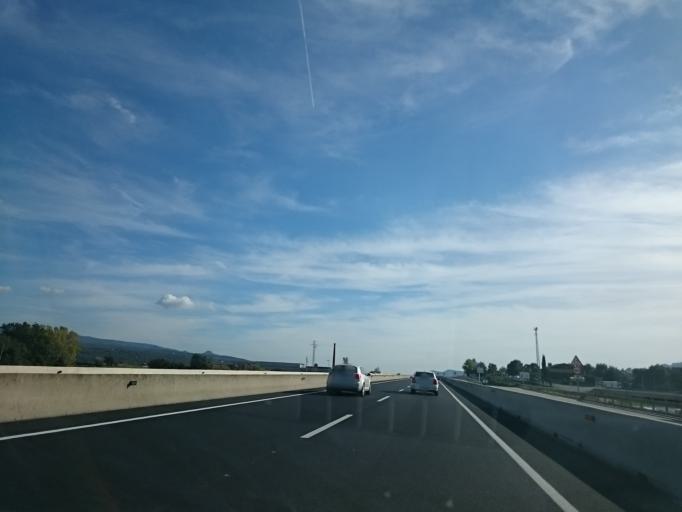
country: ES
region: Catalonia
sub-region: Provincia de Barcelona
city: Tona
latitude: 41.8417
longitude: 2.2327
